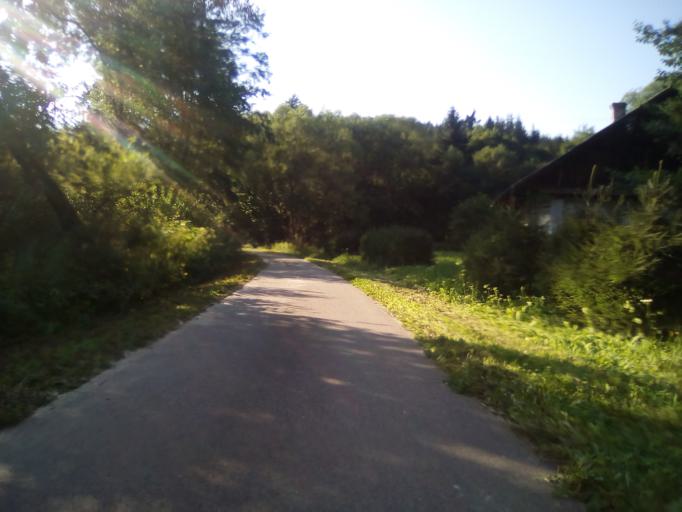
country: PL
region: Subcarpathian Voivodeship
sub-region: Powiat brzozowski
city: Domaradz
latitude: 49.8153
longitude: 21.9570
